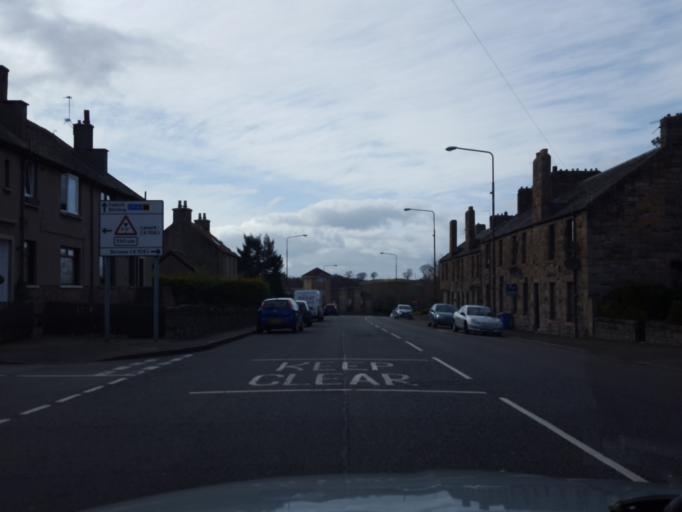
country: GB
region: Scotland
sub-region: West Lothian
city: Linlithgow
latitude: 55.9760
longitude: -3.6267
